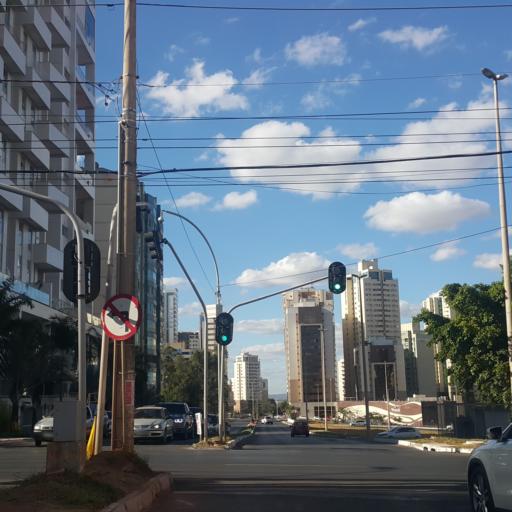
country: BR
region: Federal District
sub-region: Brasilia
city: Brasilia
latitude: -15.8405
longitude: -48.0349
